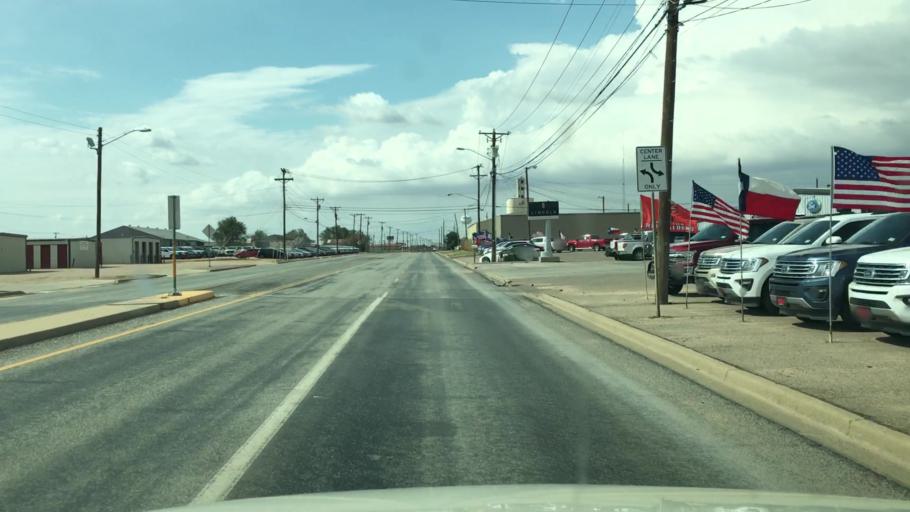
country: US
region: Texas
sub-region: Dawson County
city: Lamesa
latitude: 32.7213
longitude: -101.9455
